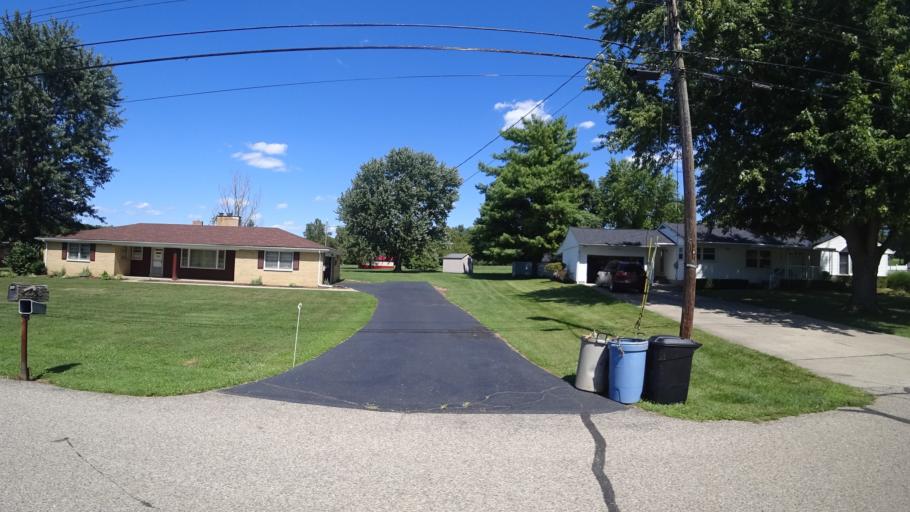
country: US
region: Ohio
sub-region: Butler County
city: New Miami
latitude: 39.4129
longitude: -84.5257
